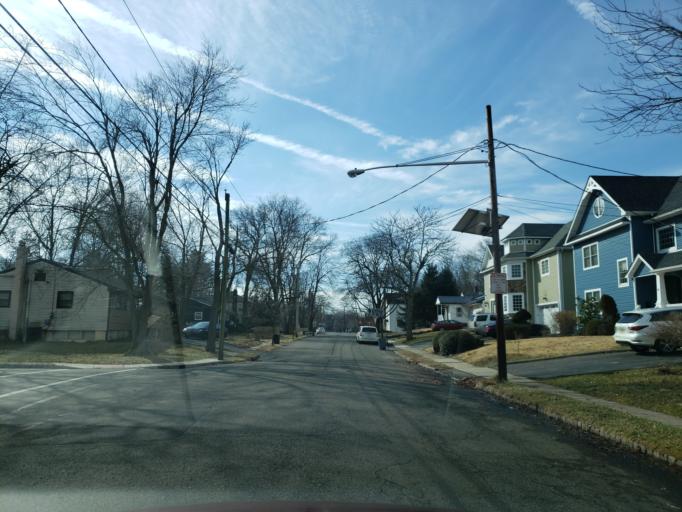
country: US
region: New Jersey
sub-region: Essex County
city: West Orange
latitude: 40.8029
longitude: -74.2607
